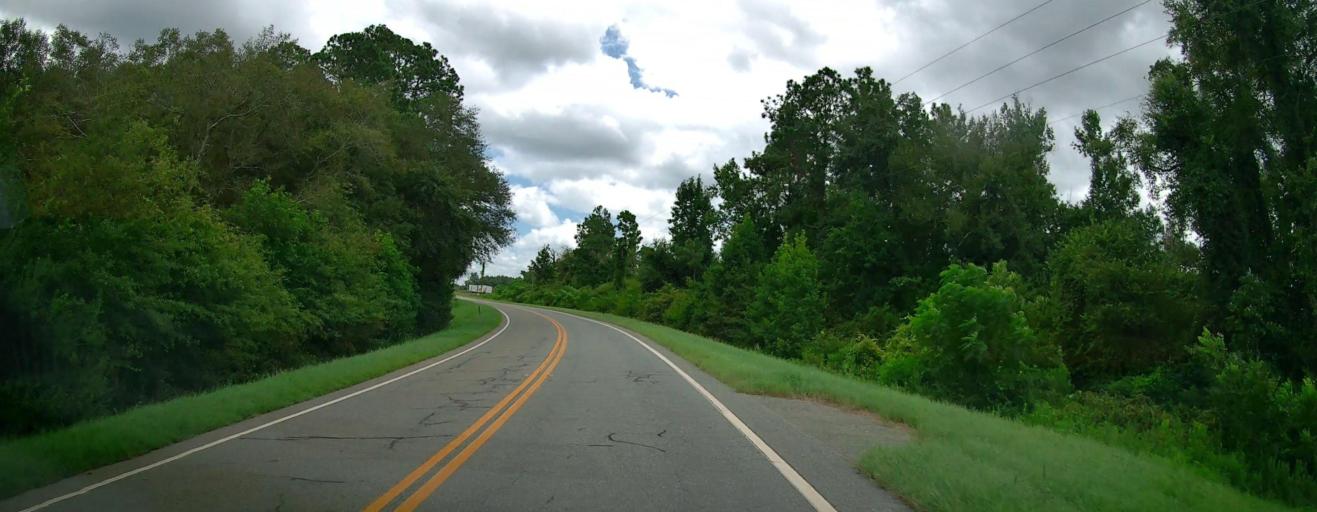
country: US
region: Georgia
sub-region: Wilcox County
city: Rochelle
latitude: 31.9965
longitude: -83.5565
